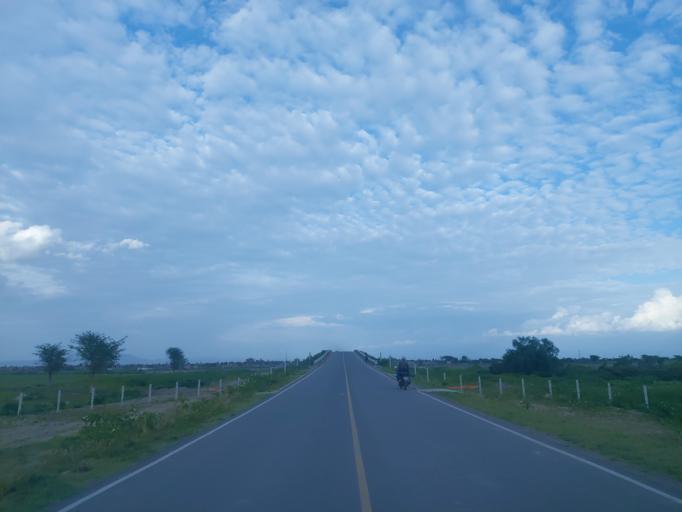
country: ET
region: Oromiya
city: Ziway
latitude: 8.1489
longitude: 38.7945
